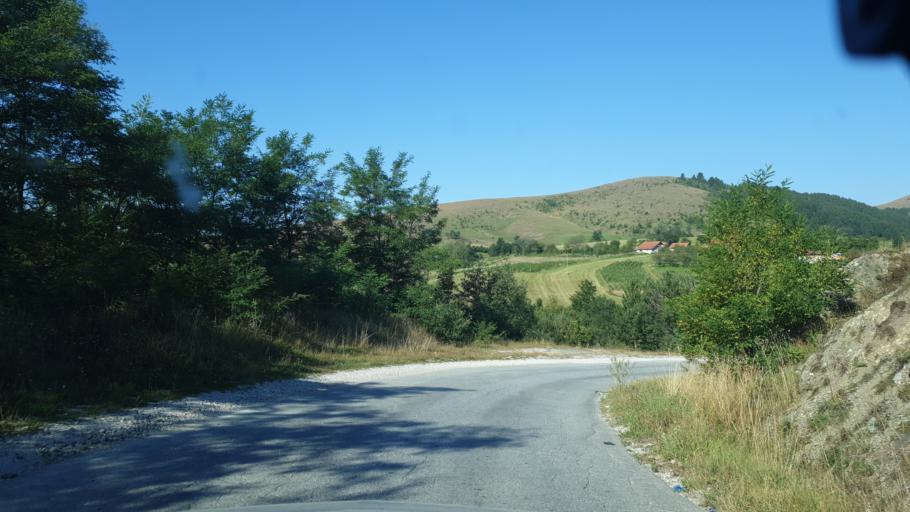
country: RS
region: Central Serbia
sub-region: Zlatiborski Okrug
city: Cajetina
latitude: 43.7195
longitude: 19.7591
